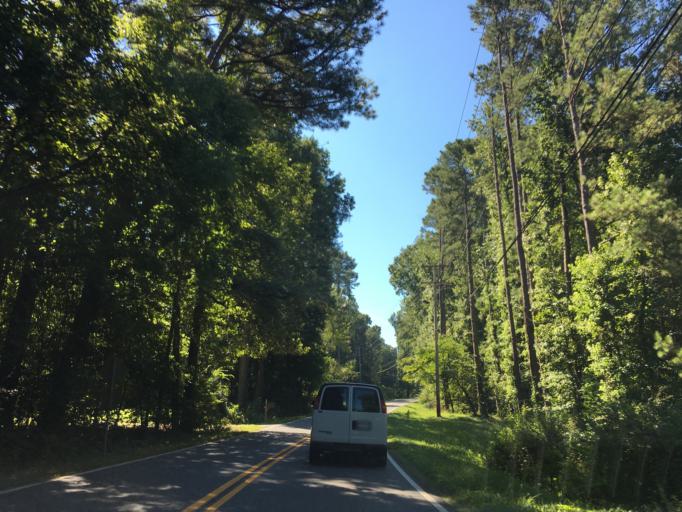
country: US
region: Georgia
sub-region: Fulton County
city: Milton
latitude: 34.1578
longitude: -84.2871
